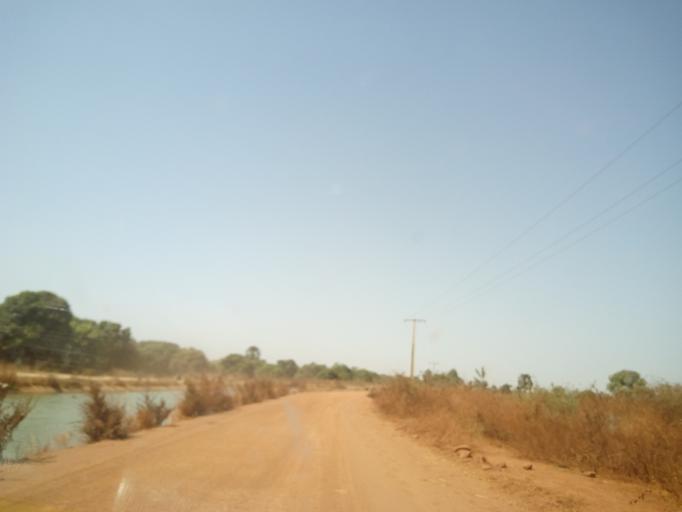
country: ML
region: Bamako
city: Bamako
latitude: 12.6230
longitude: -7.7576
